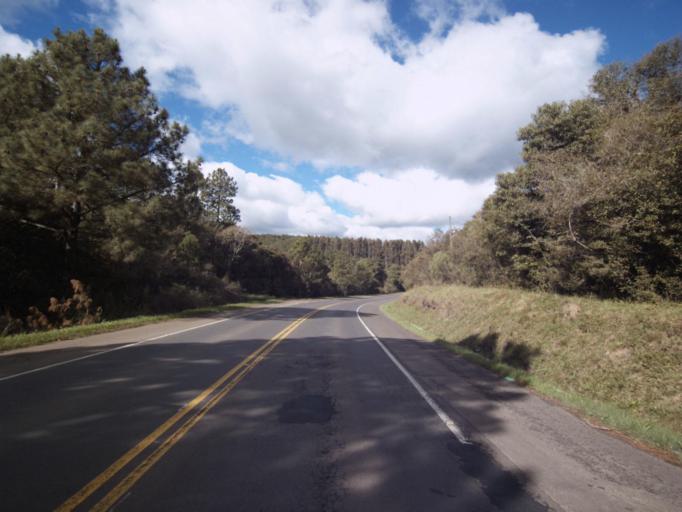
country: BR
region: Santa Catarina
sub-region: Joacaba
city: Joacaba
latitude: -27.0277
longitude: -51.7264
